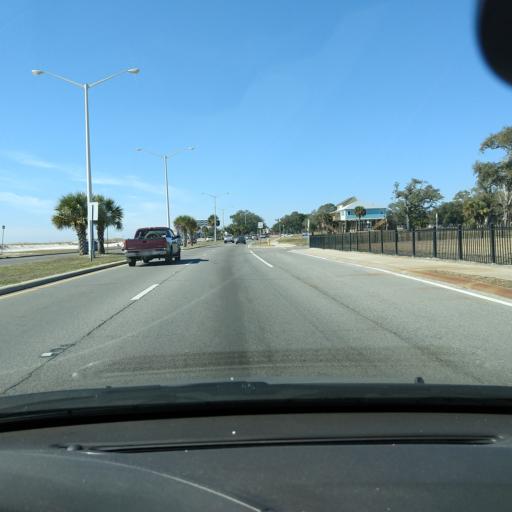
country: US
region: Mississippi
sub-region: Harrison County
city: Biloxi
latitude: 30.3934
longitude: -88.9324
